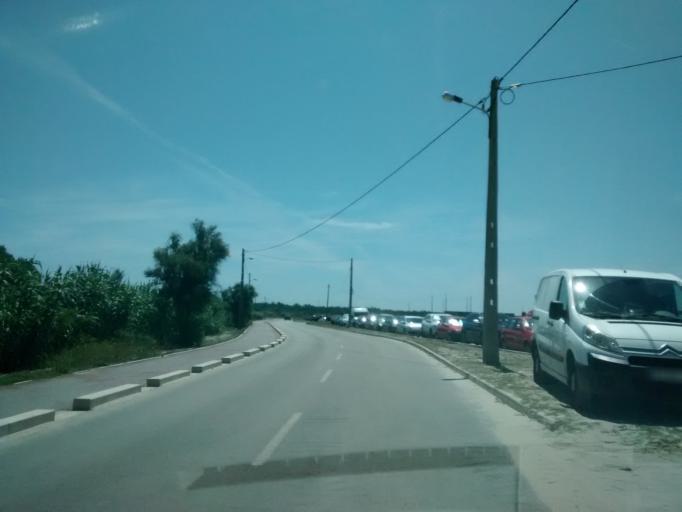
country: PT
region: Coimbra
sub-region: Mira
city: Mira
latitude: 40.4475
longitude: -8.8046
